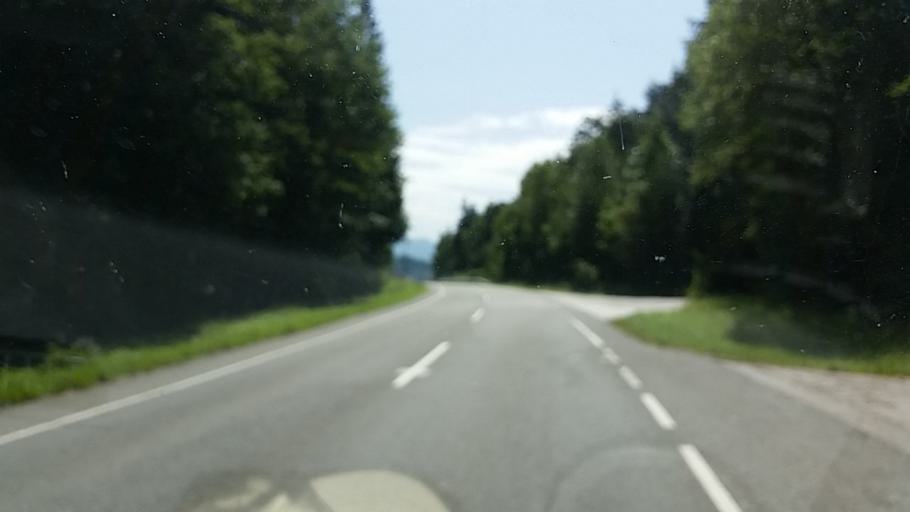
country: AT
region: Salzburg
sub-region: Politischer Bezirk Sankt Johann im Pongau
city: Werfen
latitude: 47.5156
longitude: 13.1642
